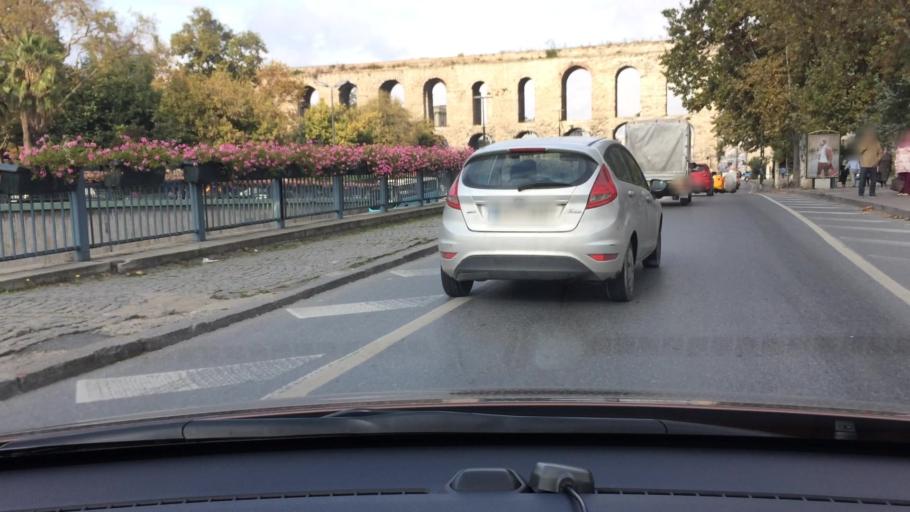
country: TR
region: Istanbul
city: Istanbul
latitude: 41.0148
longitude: 28.9548
